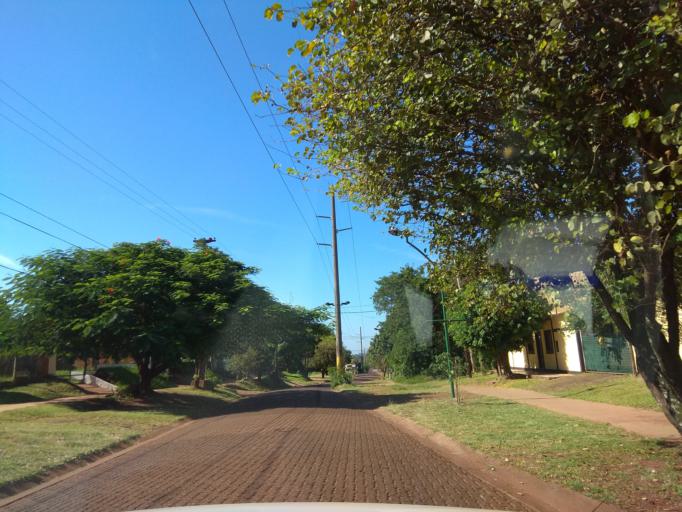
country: AR
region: Misiones
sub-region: Departamento de Capital
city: Posadas
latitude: -27.3973
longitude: -55.9170
